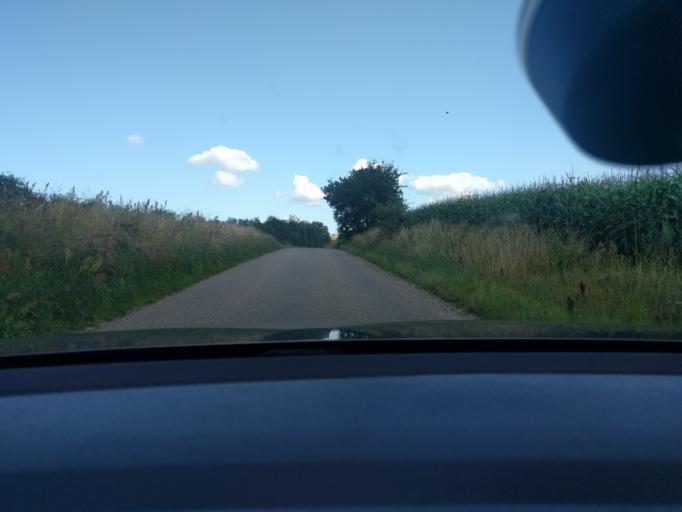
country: DK
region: Central Jutland
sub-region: Viborg Kommune
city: Viborg
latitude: 56.5234
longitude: 9.3248
